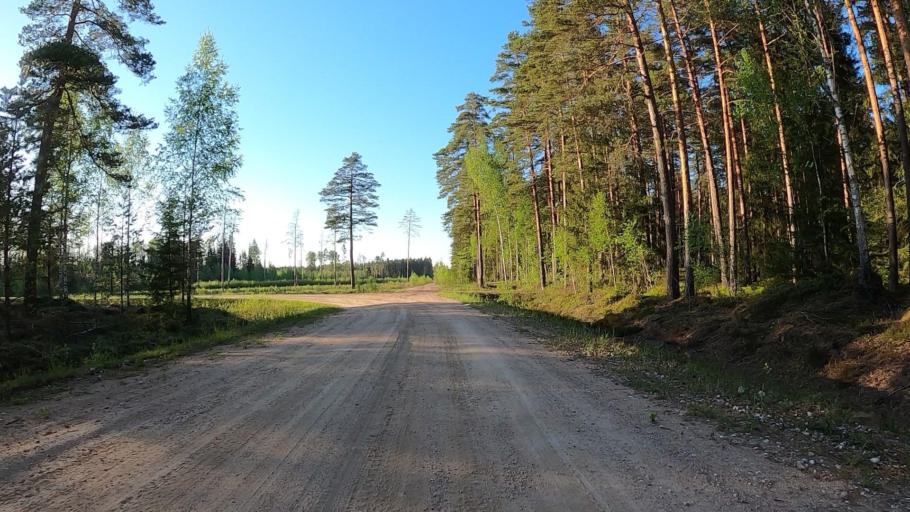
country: LV
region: Kekava
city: Kekava
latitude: 56.7677
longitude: 24.2227
